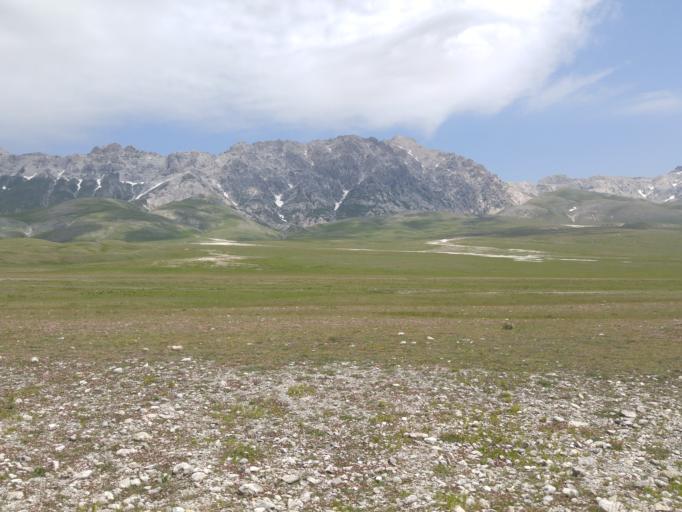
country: IT
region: Abruzzo
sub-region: Provincia dell' Aquila
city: Santo Stefano di Sessanio
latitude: 42.3995
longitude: 13.6587
